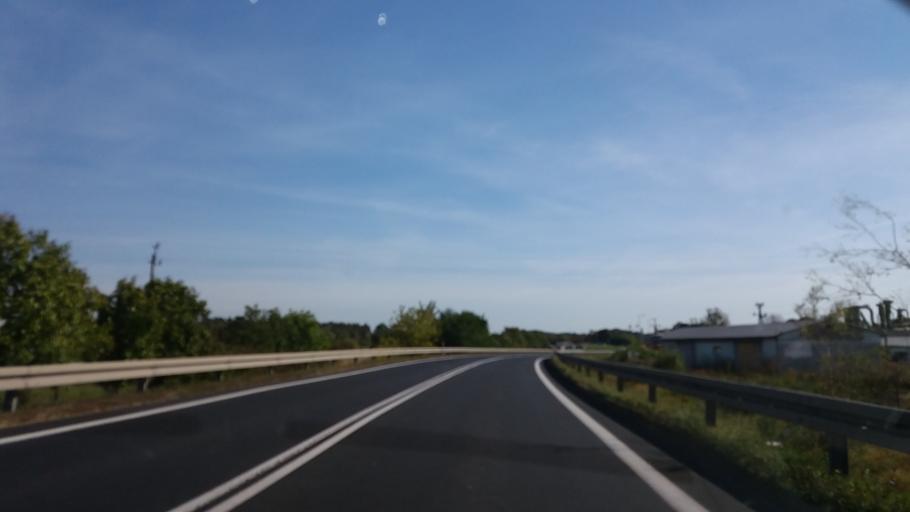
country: PL
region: Greater Poland Voivodeship
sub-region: Powiat miedzychodzki
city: Kwilcz
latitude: 52.5516
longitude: 16.1044
